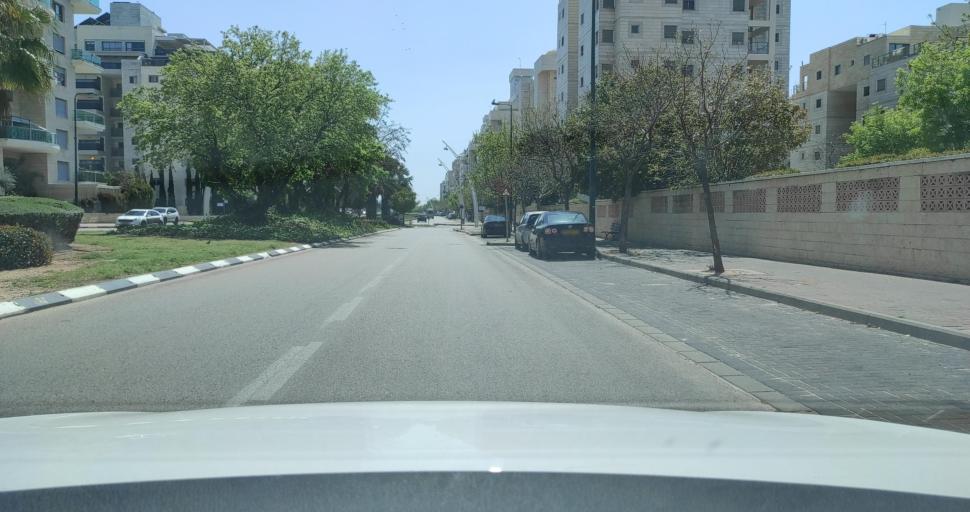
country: IL
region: Central District
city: Nordiyya
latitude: 32.3012
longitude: 34.8736
